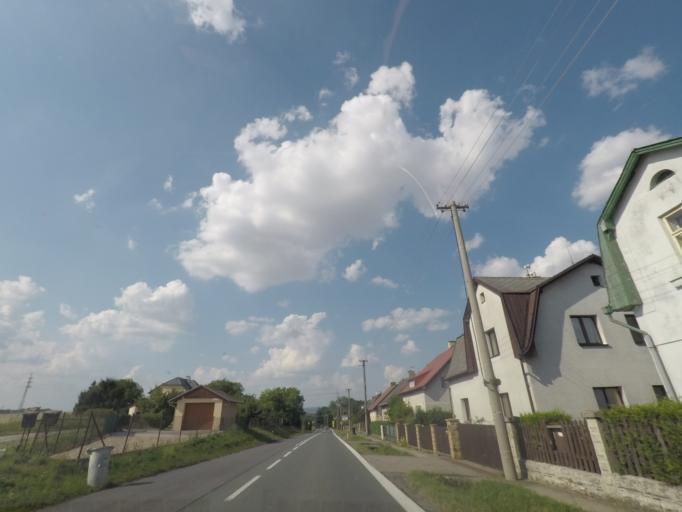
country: CZ
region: Kralovehradecky
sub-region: Okres Nachod
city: Jaromer
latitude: 50.3619
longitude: 15.9066
